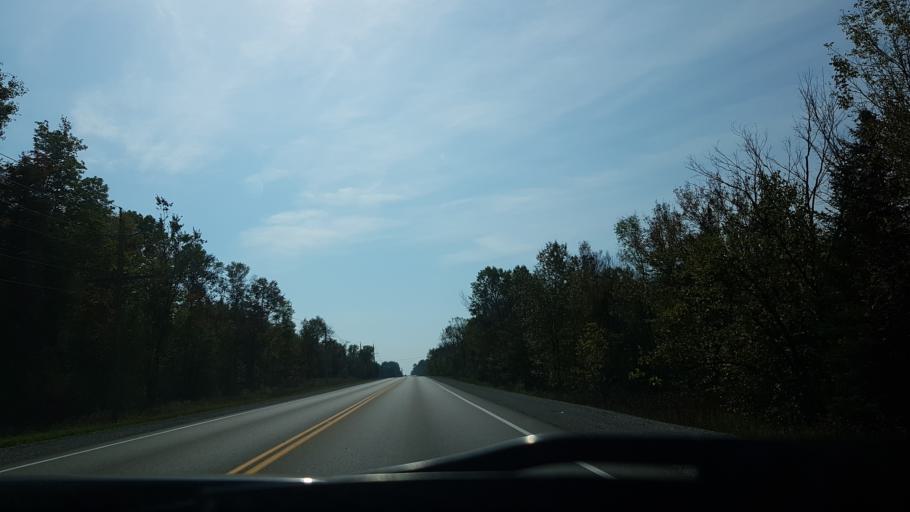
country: CA
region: Ontario
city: Orillia
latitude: 44.7365
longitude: -79.2912
